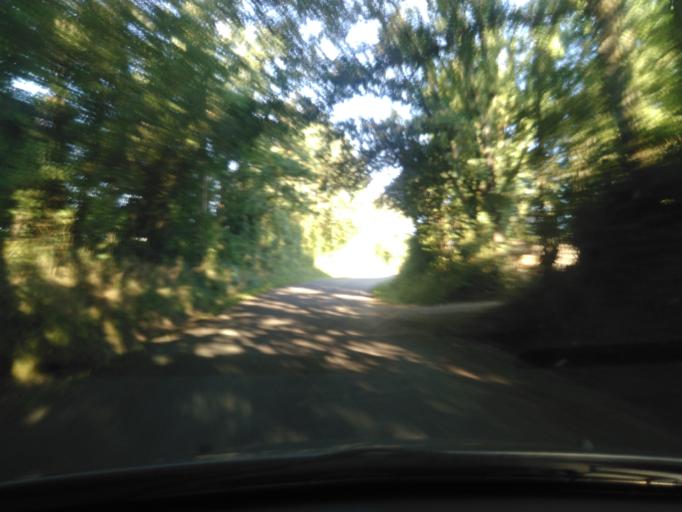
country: FR
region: Pays de la Loire
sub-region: Departement de la Vendee
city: Dompierre-sur-Yon
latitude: 46.7027
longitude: -1.4088
